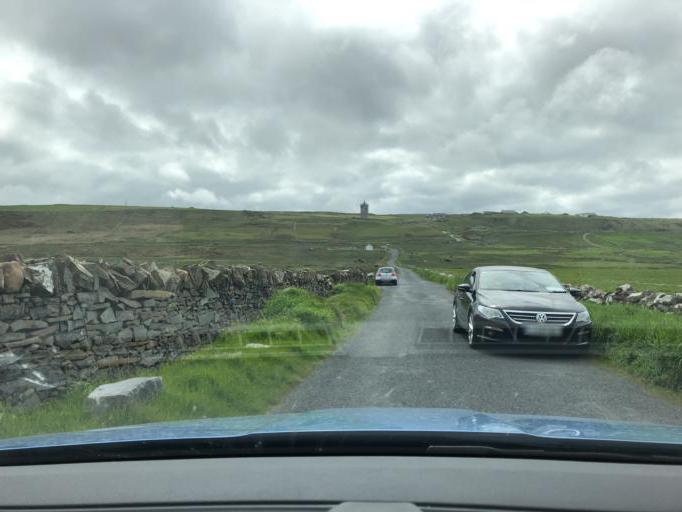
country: IE
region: Connaught
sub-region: County Galway
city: Bearna
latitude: 53.0093
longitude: -9.3888
